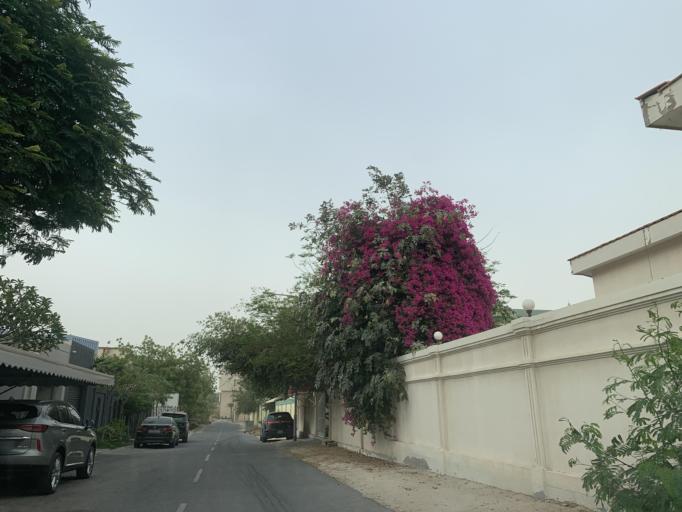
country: BH
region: Central Governorate
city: Madinat Hamad
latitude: 26.1394
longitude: 50.5200
